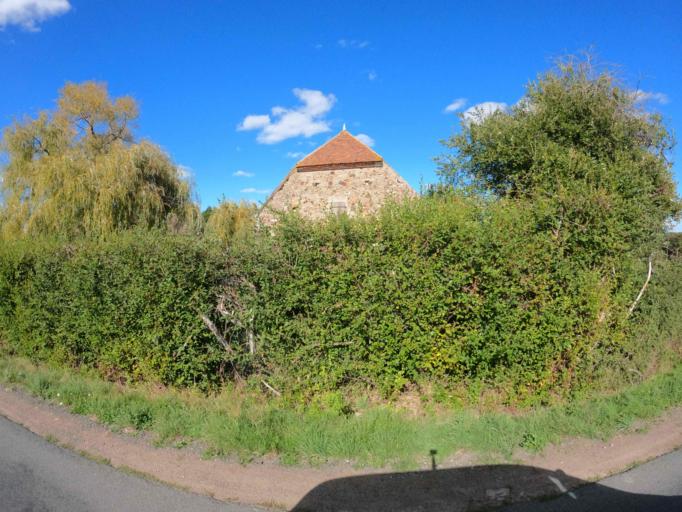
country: FR
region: Auvergne
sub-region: Departement de l'Allier
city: Doyet
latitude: 46.3895
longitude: 2.7628
